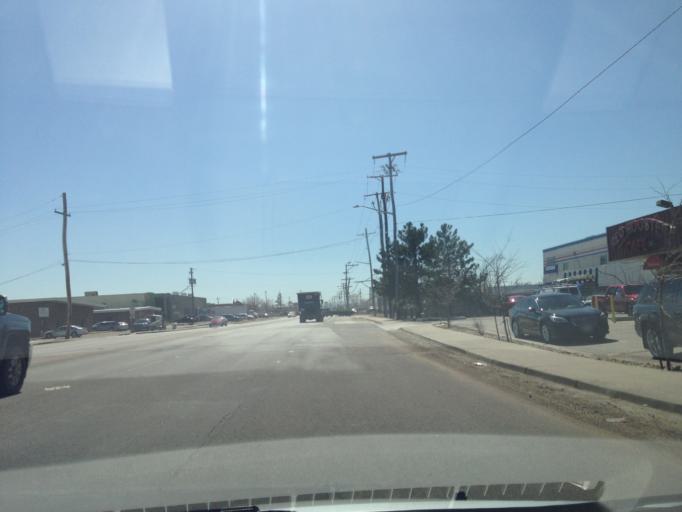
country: US
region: Colorado
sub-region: Adams County
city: Twin Lakes
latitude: 39.8015
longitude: -104.9782
